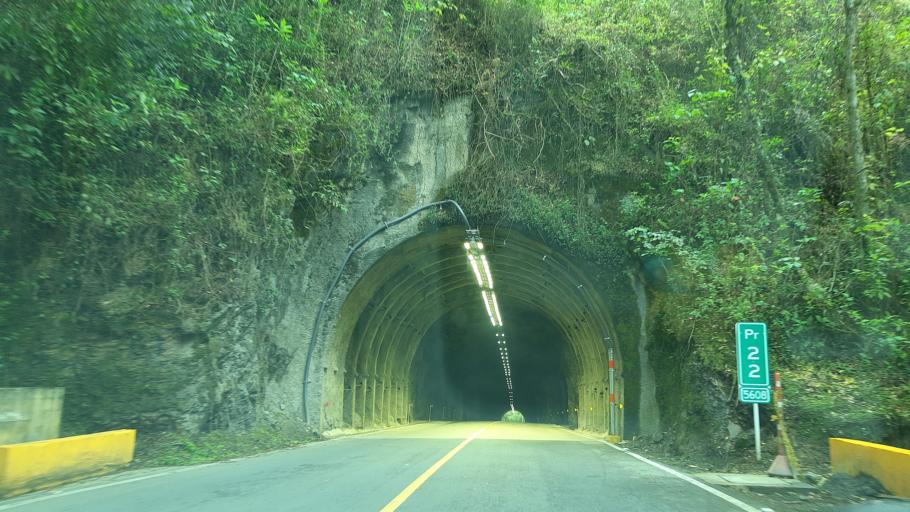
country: CO
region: Boyaca
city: Somondoco
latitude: 4.9877
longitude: -73.3493
